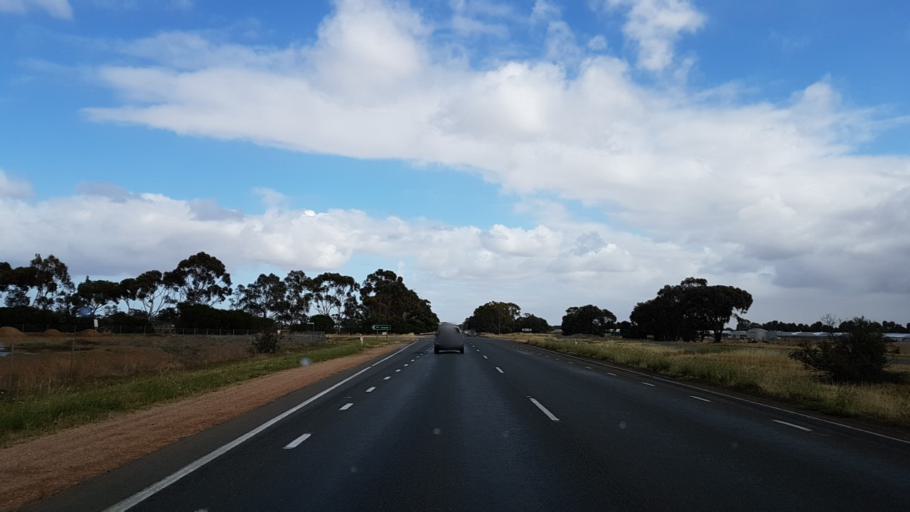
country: AU
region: South Australia
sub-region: Mallala
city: Two Wells
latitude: -34.6255
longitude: 138.5238
